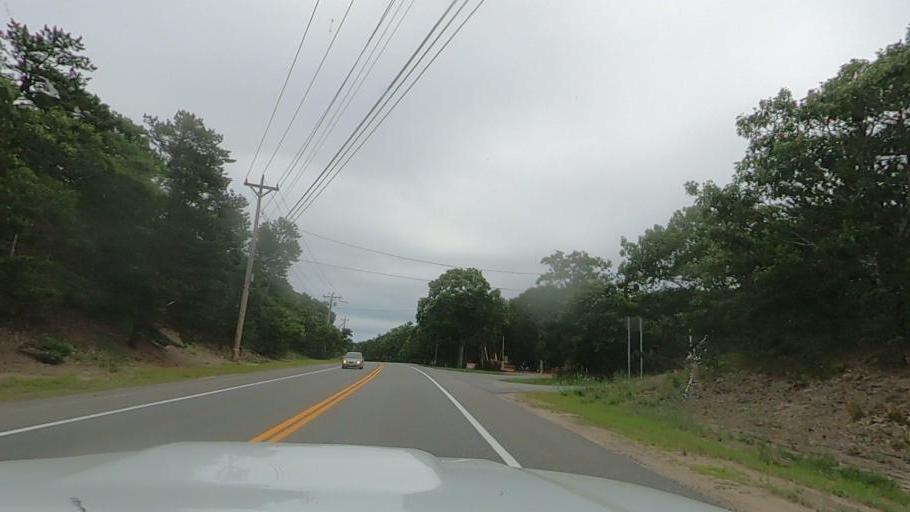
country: US
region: Massachusetts
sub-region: Barnstable County
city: Truro
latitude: 41.9810
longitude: -70.0431
